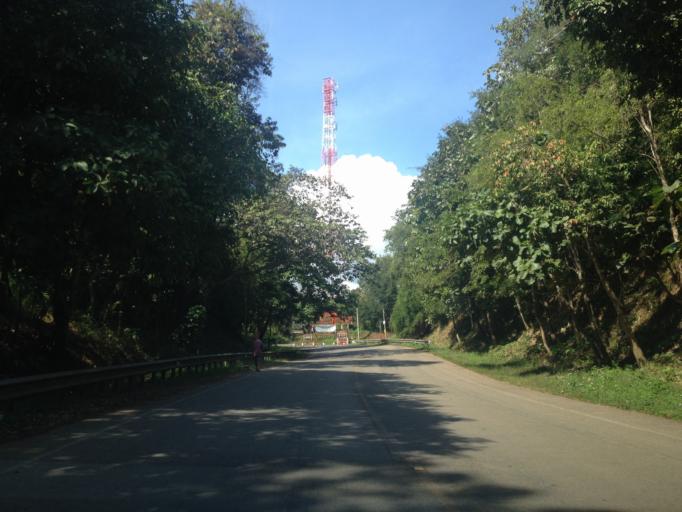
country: TH
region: Chiang Mai
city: Samoeng
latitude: 18.8061
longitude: 98.8293
